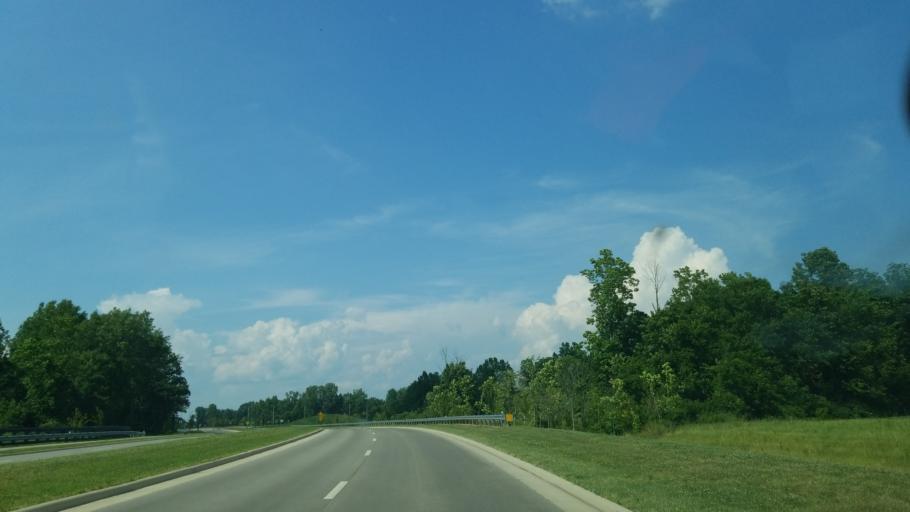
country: US
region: Ohio
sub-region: Delaware County
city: Delaware
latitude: 40.2498
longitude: -83.0918
